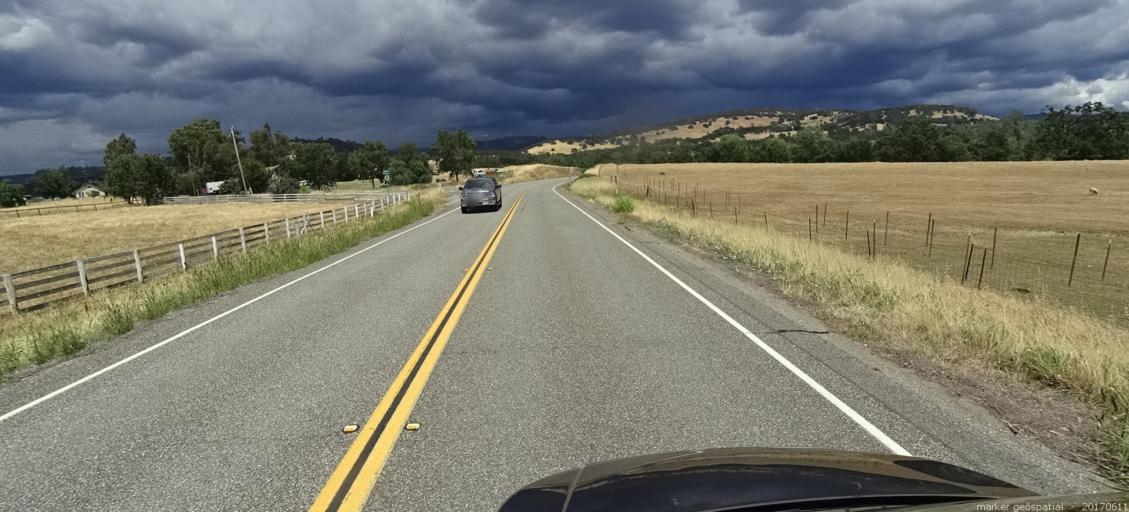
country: US
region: California
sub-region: Butte County
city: Paradise
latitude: 39.6540
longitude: -121.5844
